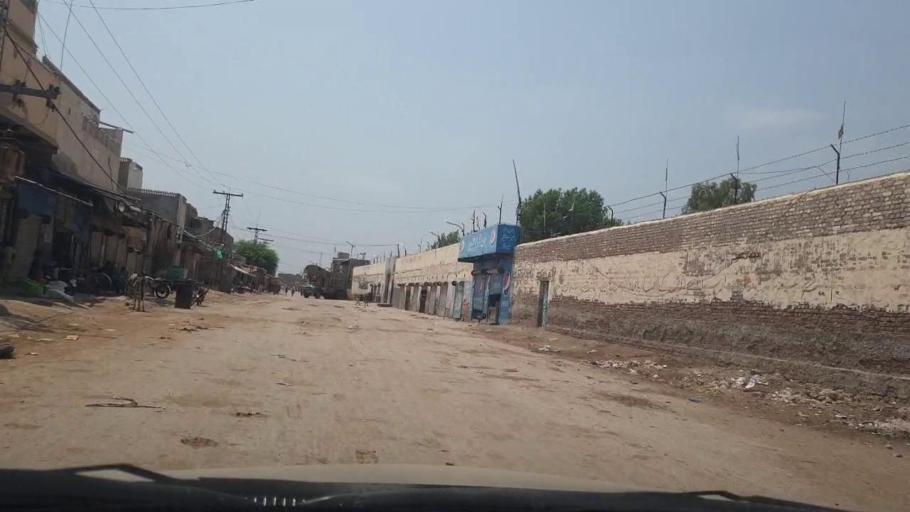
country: PK
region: Sindh
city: Ratodero
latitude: 27.7275
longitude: 68.2827
